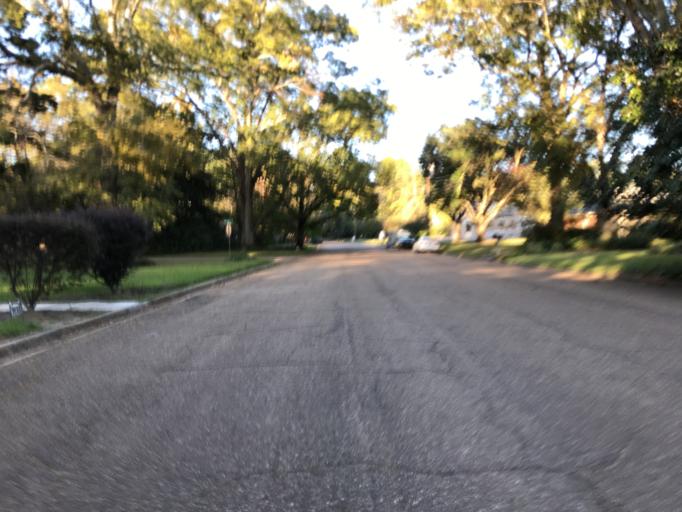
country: US
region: Mississippi
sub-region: Rankin County
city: Flowood
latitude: 32.3439
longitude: -90.1687
